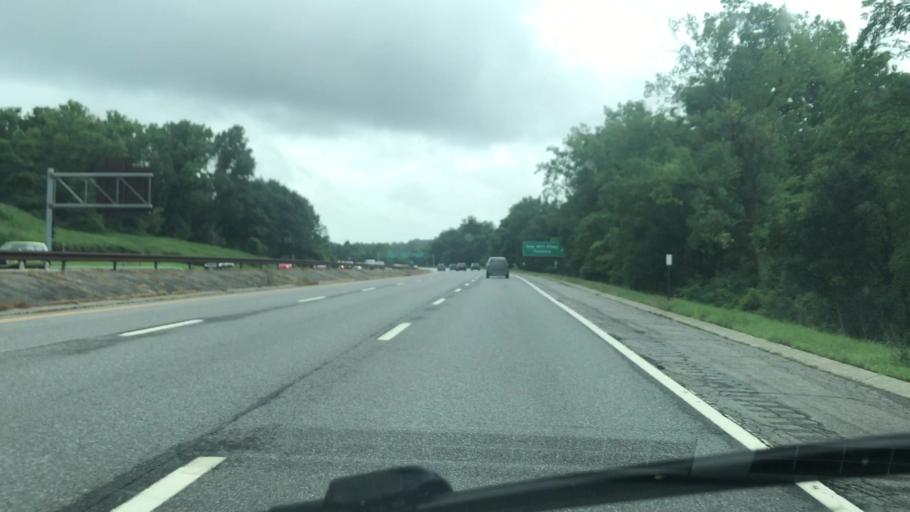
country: US
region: New York
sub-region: Westchester County
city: Hawthorne
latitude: 41.1165
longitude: -73.8063
